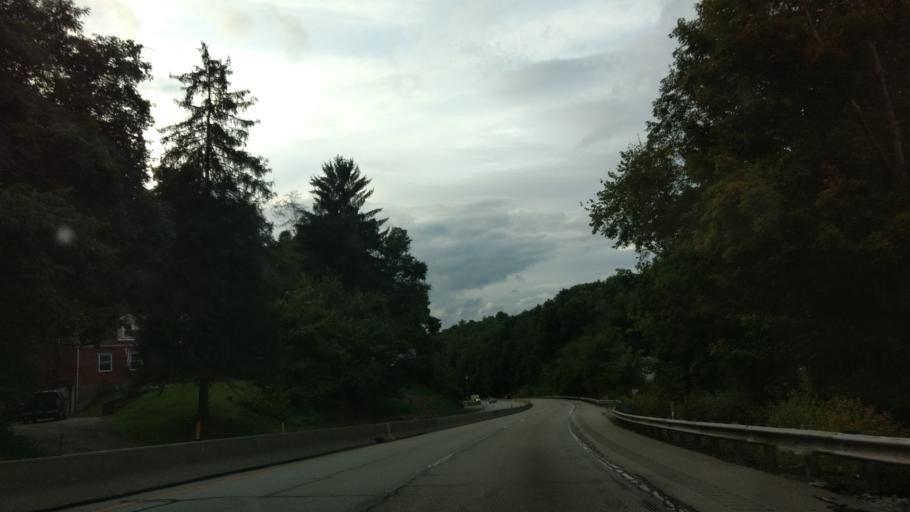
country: US
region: Pennsylvania
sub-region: Allegheny County
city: Elizabeth
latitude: 40.2425
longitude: -79.8712
